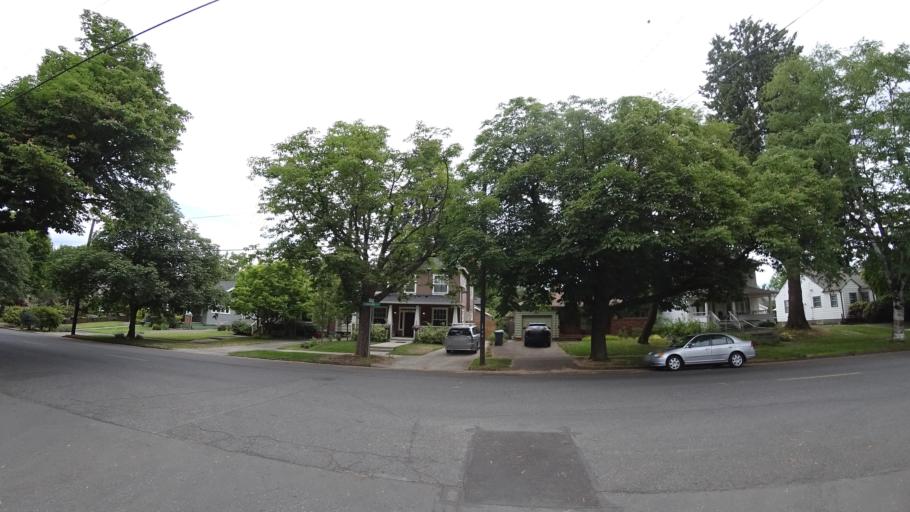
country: US
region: Oregon
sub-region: Multnomah County
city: Portland
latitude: 45.5783
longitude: -122.7081
